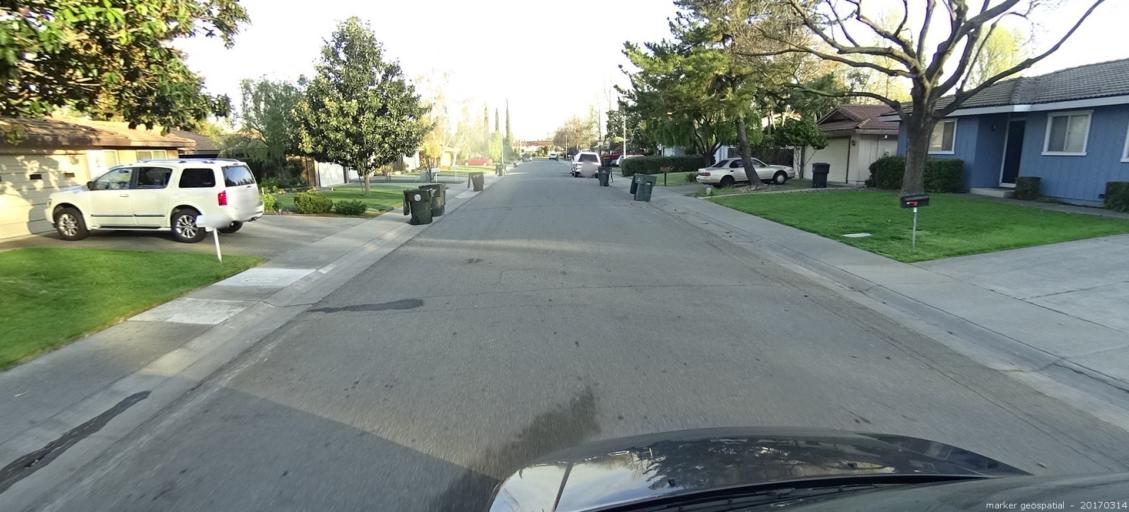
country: US
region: California
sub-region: Yolo County
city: West Sacramento
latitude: 38.5047
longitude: -121.5409
